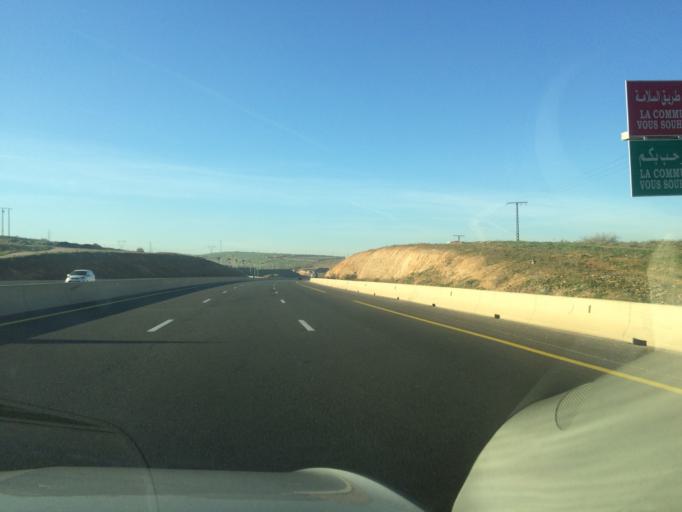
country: DZ
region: Chlef
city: Oued Sly
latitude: 36.0797
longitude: 1.1839
